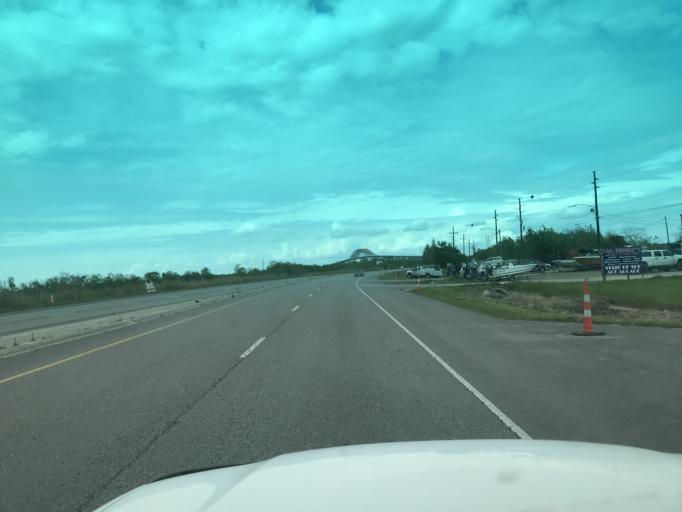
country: US
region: Louisiana
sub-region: Saint Bernard Parish
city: Chalmette
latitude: 29.9877
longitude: -89.9436
